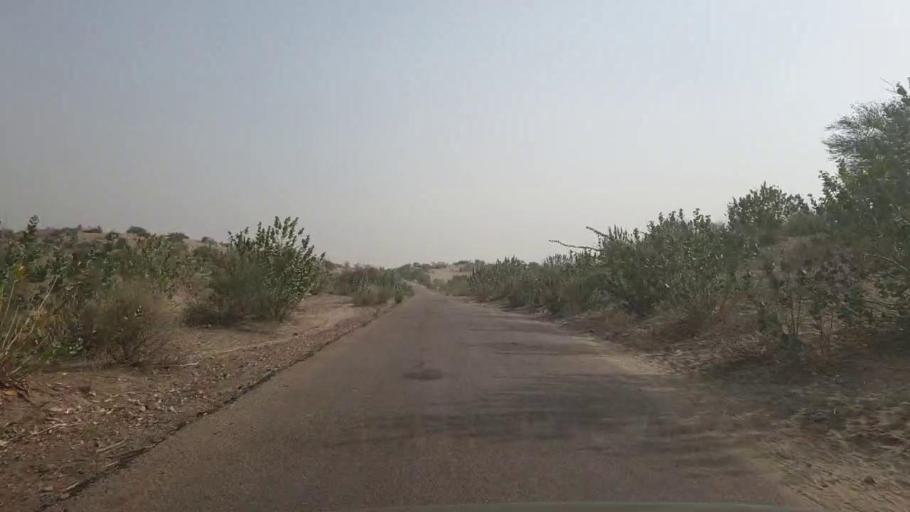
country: PK
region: Sindh
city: Chor
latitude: 25.5317
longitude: 69.9603
